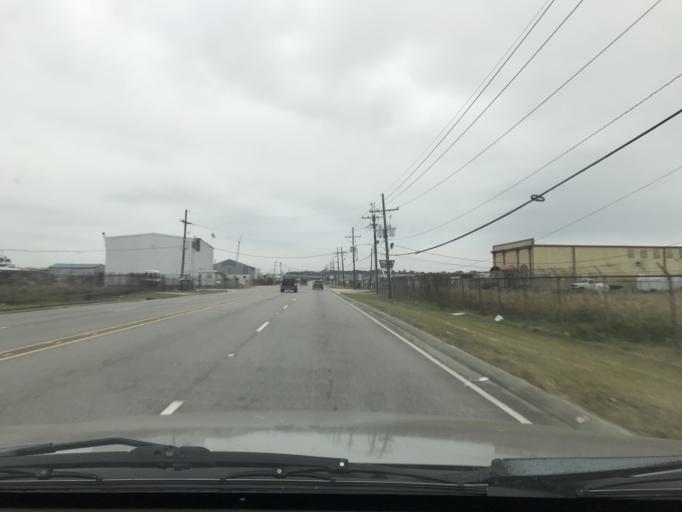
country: US
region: Louisiana
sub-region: Jefferson Parish
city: Woodmere
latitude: 29.8790
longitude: -90.0750
